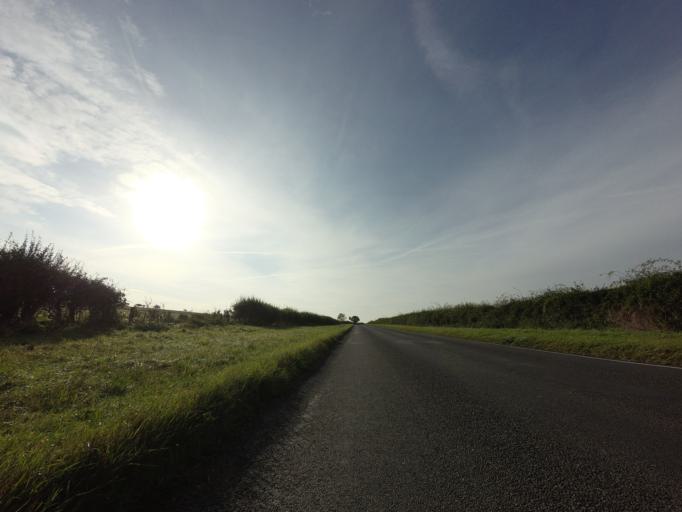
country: GB
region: England
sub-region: Cambridgeshire
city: Harston
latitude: 52.1352
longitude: 0.0999
